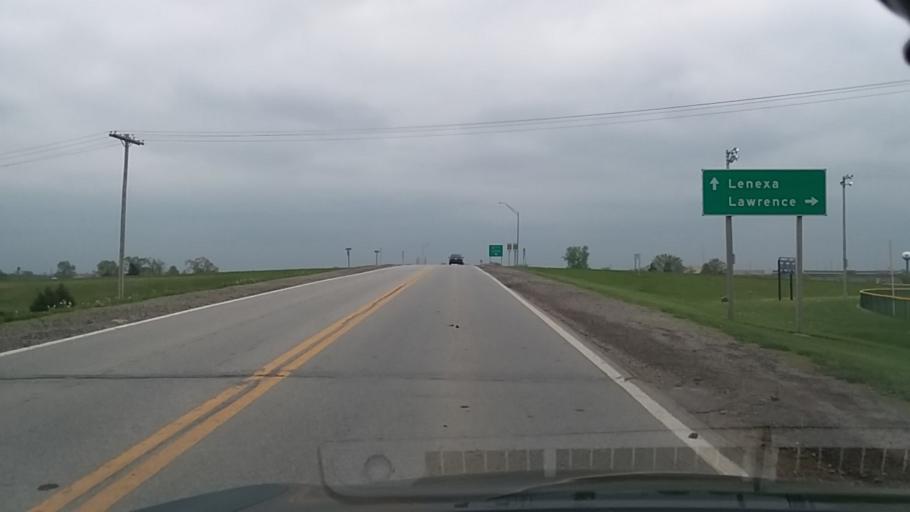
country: US
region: Kansas
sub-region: Douglas County
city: Eudora
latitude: 38.9315
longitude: -95.0955
